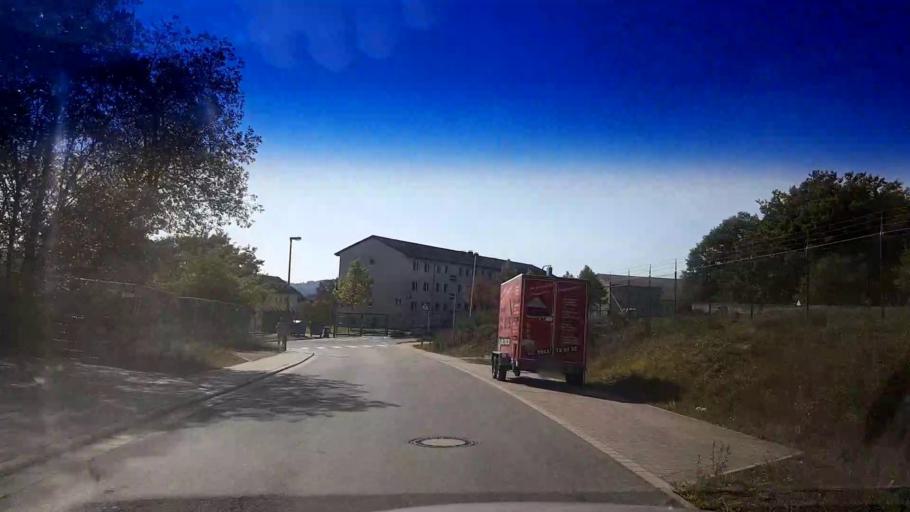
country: DE
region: Bavaria
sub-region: Upper Franconia
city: Memmelsdorf
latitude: 49.9055
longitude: 10.9374
